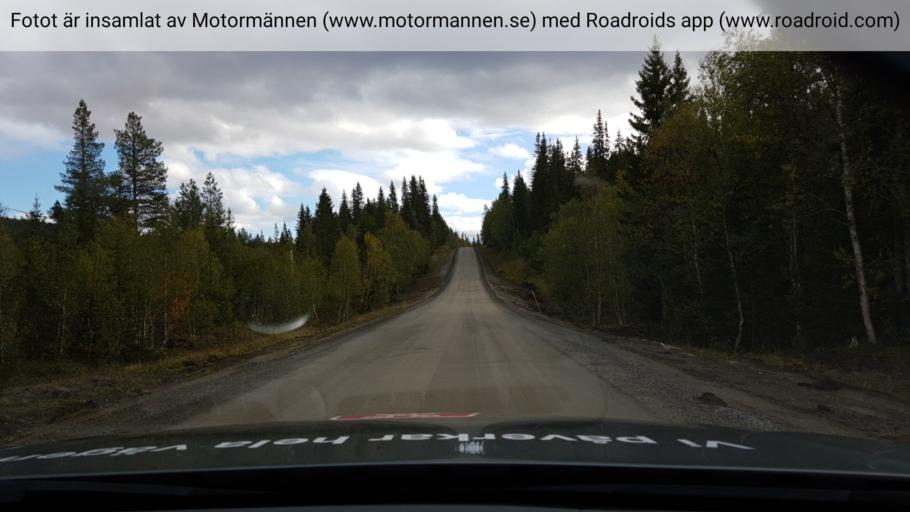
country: SE
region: Jaemtland
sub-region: Are Kommun
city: Are
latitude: 63.7164
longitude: 12.6151
